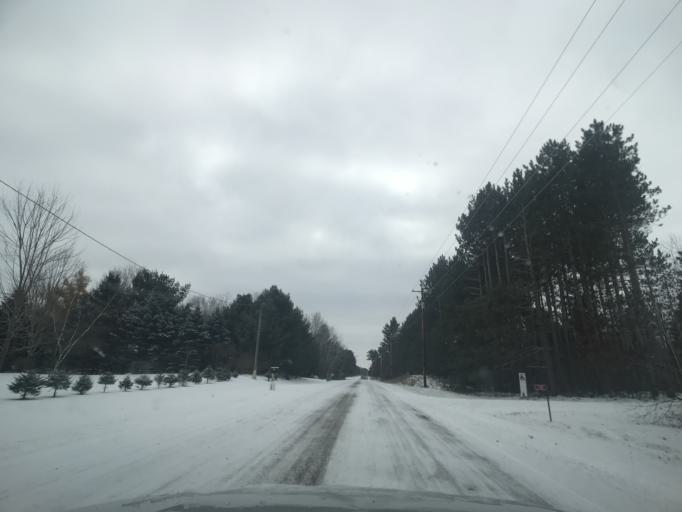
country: US
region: Wisconsin
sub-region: Brown County
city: Suamico
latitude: 44.7016
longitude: -88.1011
